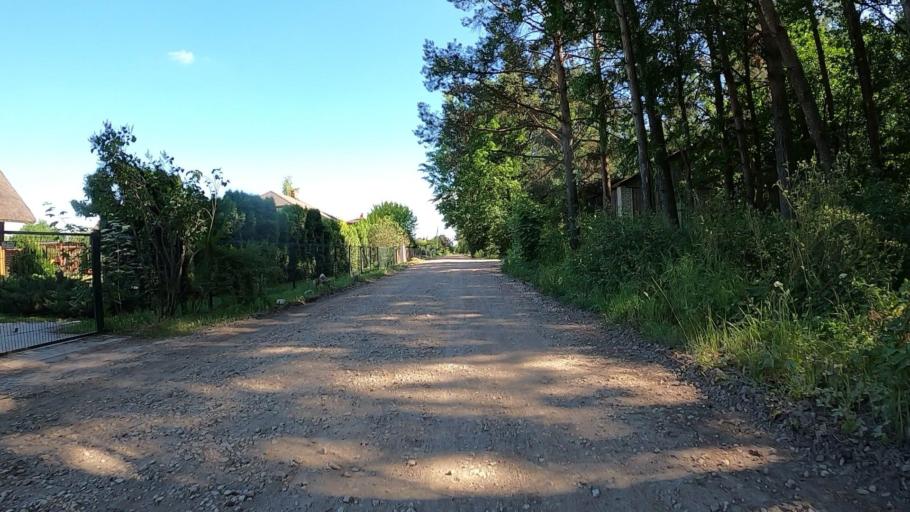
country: LV
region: Stopini
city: Ulbroka
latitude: 56.9093
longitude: 24.3138
